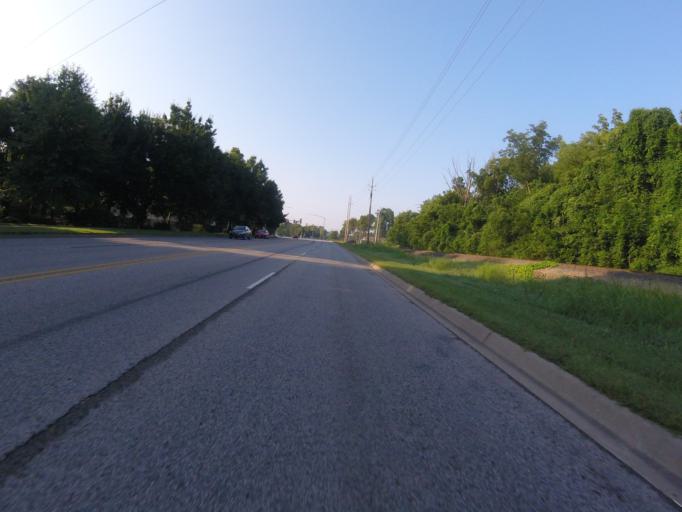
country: US
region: Arkansas
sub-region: Washington County
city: Johnson
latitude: 36.1039
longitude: -94.1637
